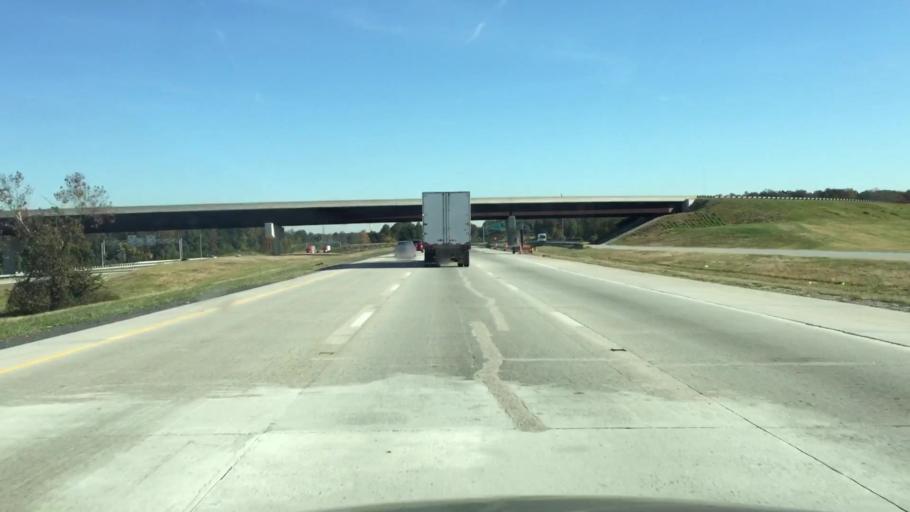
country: US
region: North Carolina
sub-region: Randolph County
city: Archdale
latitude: 35.9271
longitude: -79.9275
